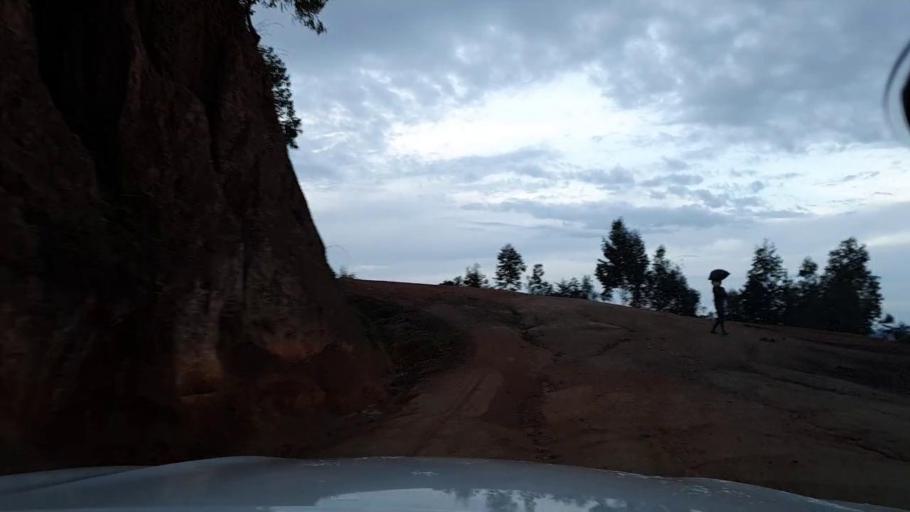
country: BI
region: Kayanza
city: Kayanza
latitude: -2.7173
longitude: 29.5435
